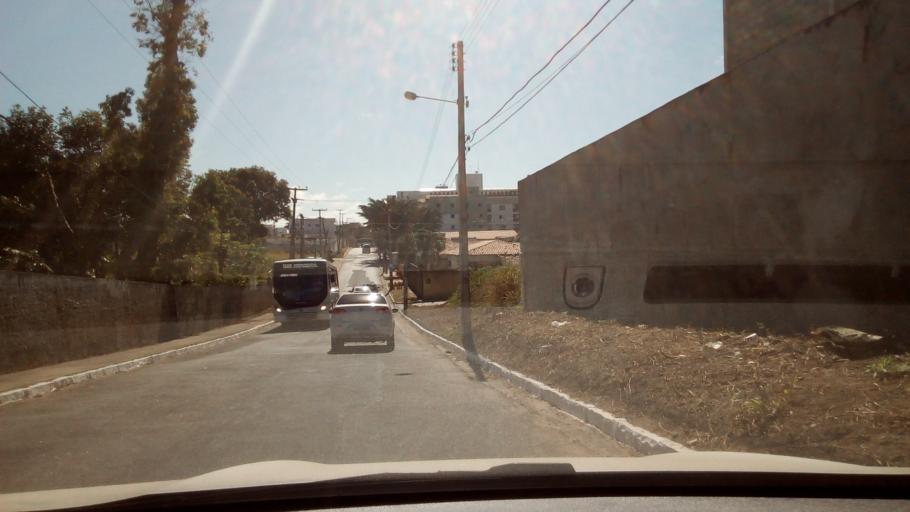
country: BR
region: Paraiba
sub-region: Joao Pessoa
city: Joao Pessoa
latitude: -7.1553
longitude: -34.8561
